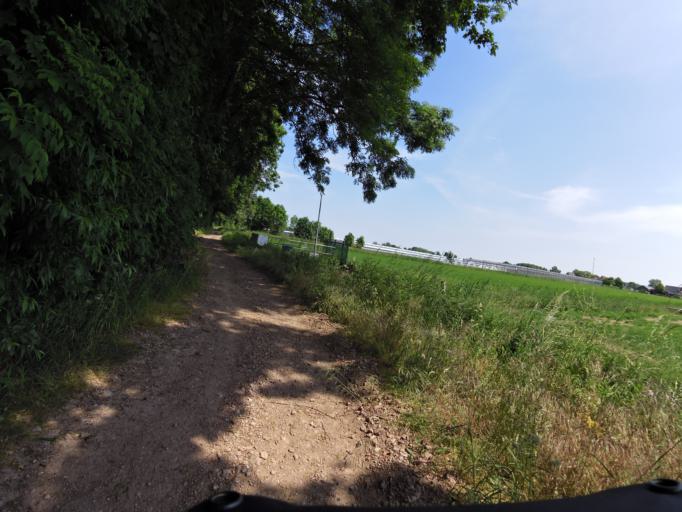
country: NL
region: North Brabant
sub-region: Gemeente Aalburg
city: Aalburg
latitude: 51.7934
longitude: 5.0946
